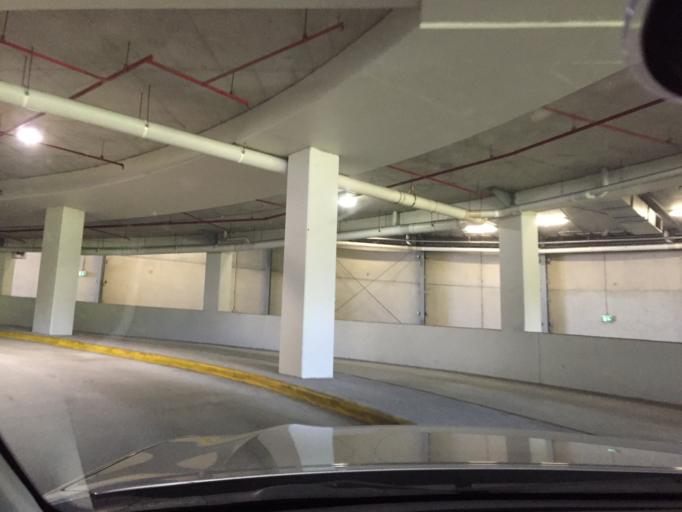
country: AU
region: Queensland
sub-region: Gold Coast
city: Surfers Paradise
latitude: -28.0271
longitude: 153.4282
